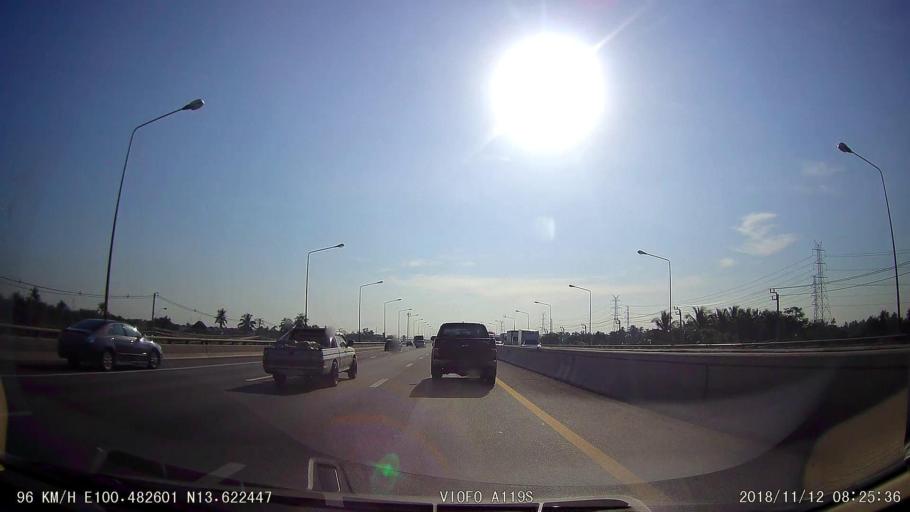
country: TH
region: Bangkok
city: Thung Khru
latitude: 13.6224
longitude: 100.4829
